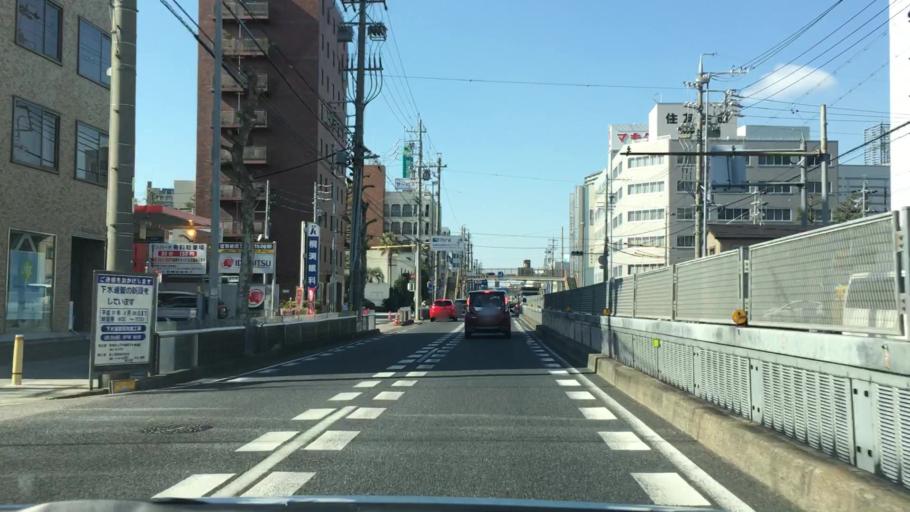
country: JP
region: Aichi
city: Okazaki
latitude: 34.9560
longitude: 137.1676
